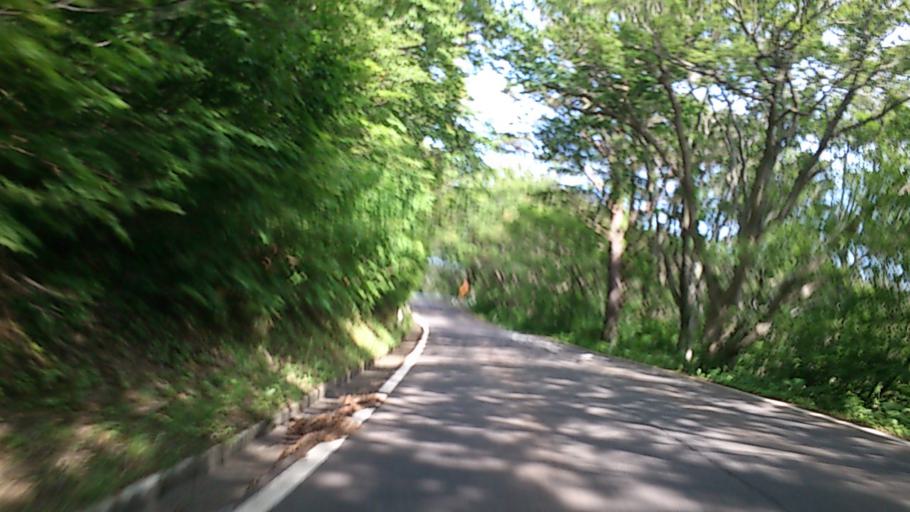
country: JP
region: Aomori
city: Aomori Shi
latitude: 40.7150
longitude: 140.8183
